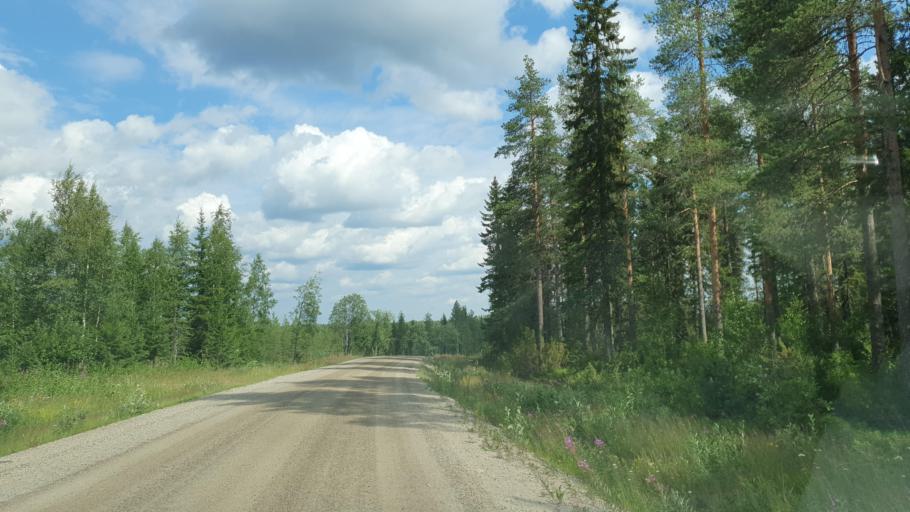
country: FI
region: Kainuu
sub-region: Kehys-Kainuu
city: Kuhmo
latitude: 64.4803
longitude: 29.5913
